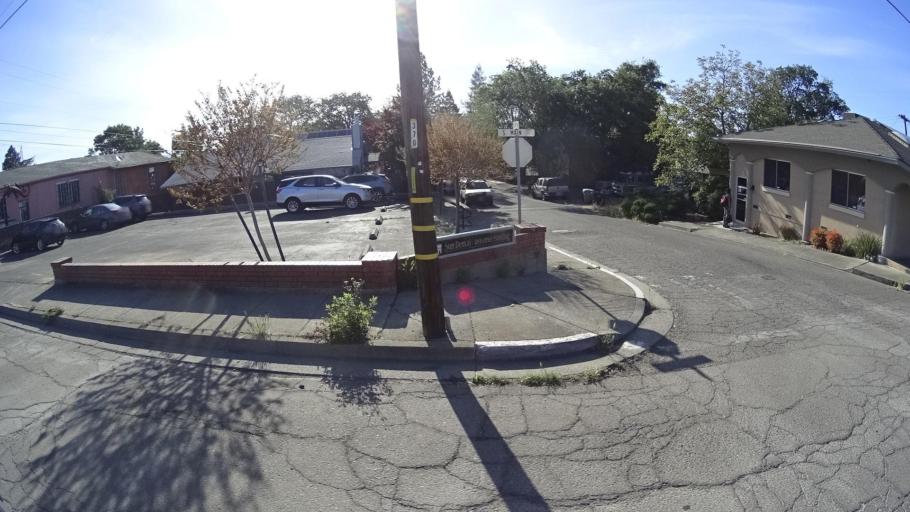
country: US
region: California
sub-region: Lake County
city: Lakeport
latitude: 39.0363
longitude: -122.9154
